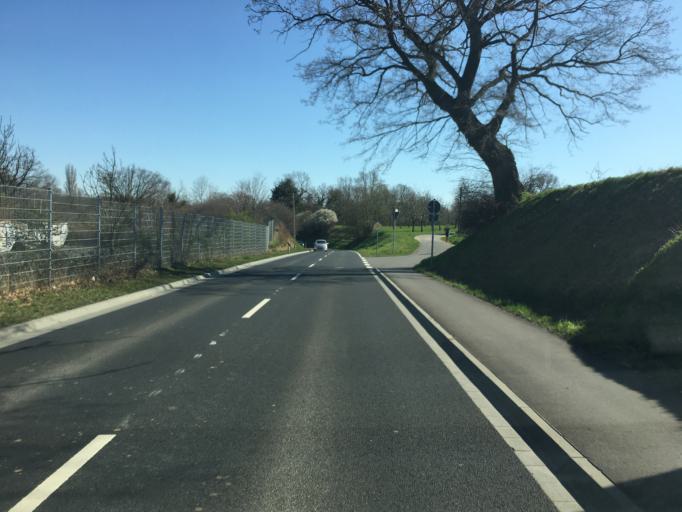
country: DE
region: North Rhine-Westphalia
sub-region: Regierungsbezirk Koln
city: Kreuzau
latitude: 50.7526
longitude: 6.4785
